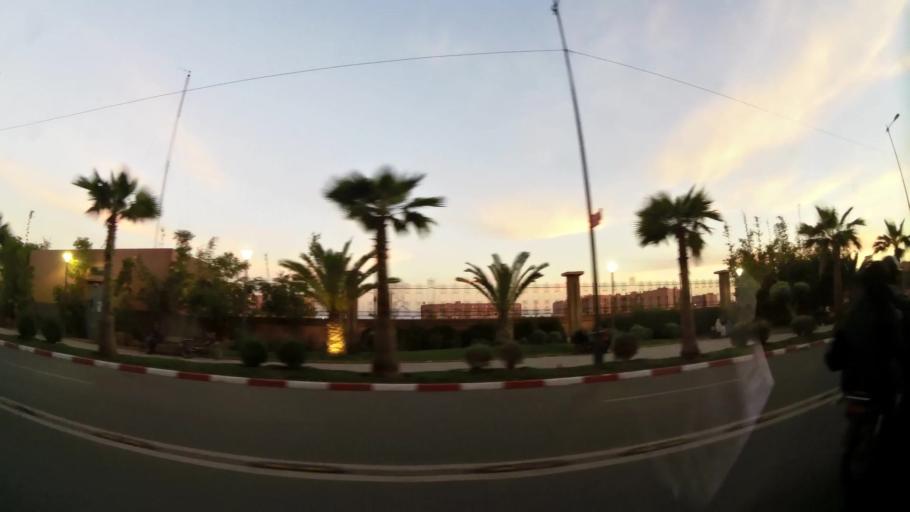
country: MA
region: Marrakech-Tensift-Al Haouz
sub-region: Marrakech
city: Marrakesh
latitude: 31.6403
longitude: -8.0010
